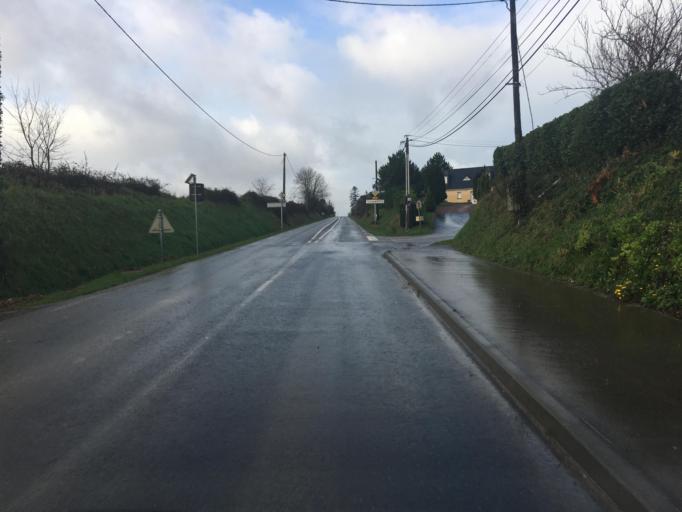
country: FR
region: Lower Normandy
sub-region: Departement de la Manche
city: Saint-Pierre-Eglise
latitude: 49.6709
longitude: -1.3396
